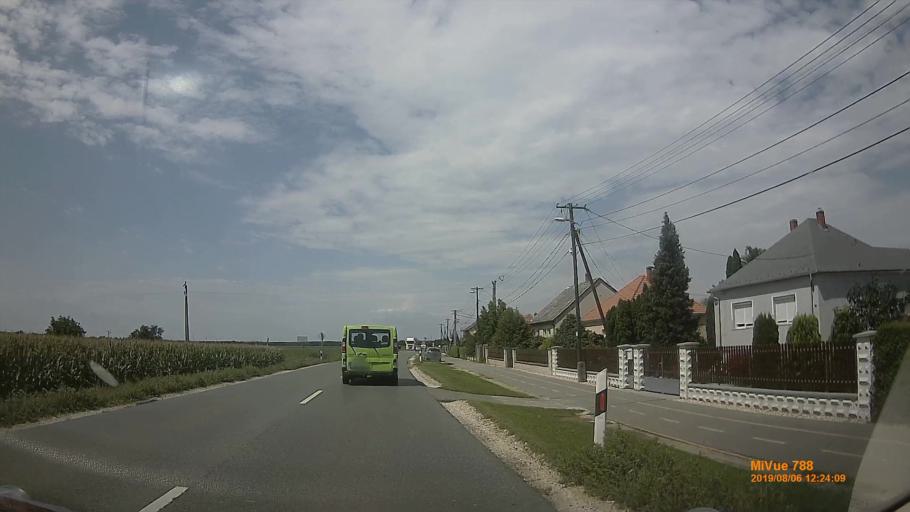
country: HU
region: Vas
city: Taplanszentkereszt
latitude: 47.1916
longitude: 16.7021
